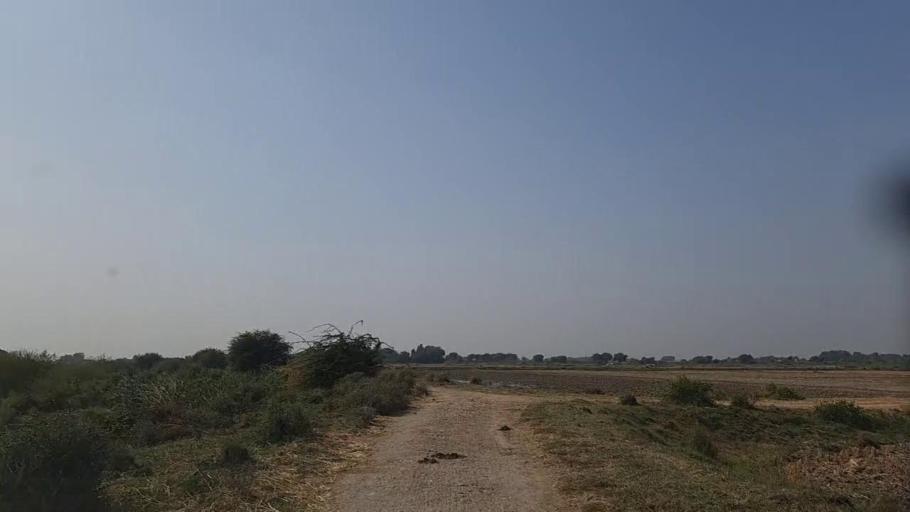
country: PK
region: Sindh
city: Mirpur Batoro
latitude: 24.5860
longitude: 68.1357
